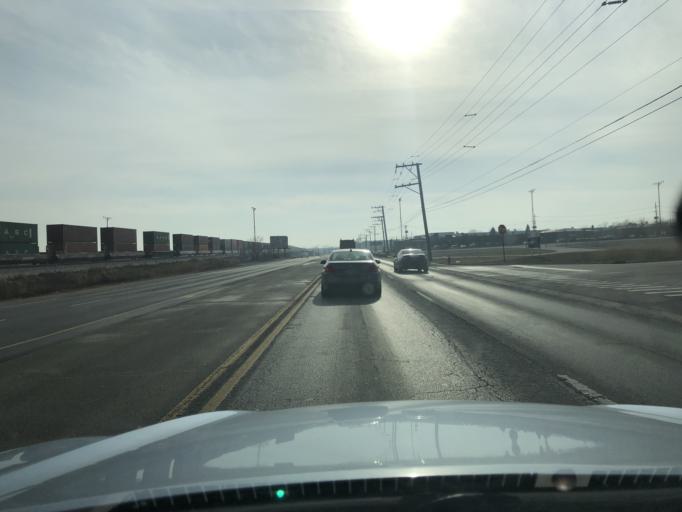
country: US
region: Illinois
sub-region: DuPage County
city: Bensenville
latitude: 41.9670
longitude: -87.9397
